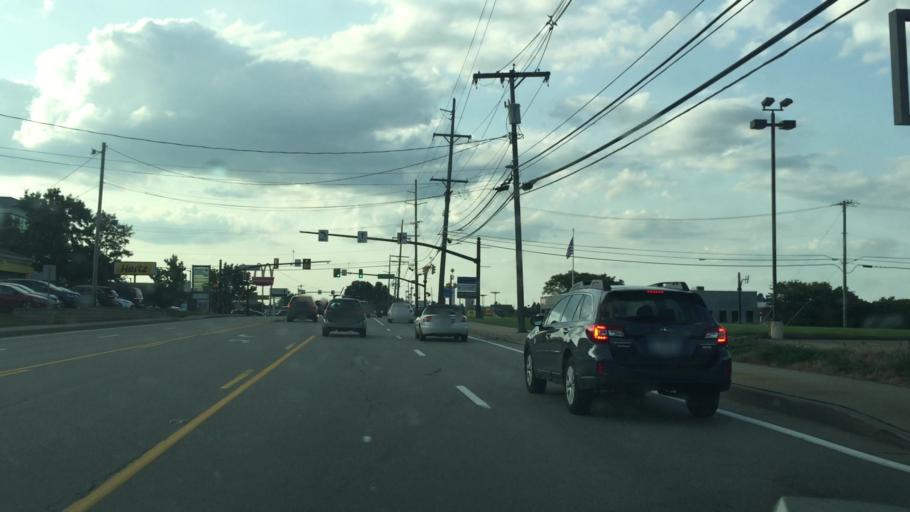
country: US
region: Pennsylvania
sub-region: Allegheny County
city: Bradford Woods
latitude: 40.6090
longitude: -80.0528
